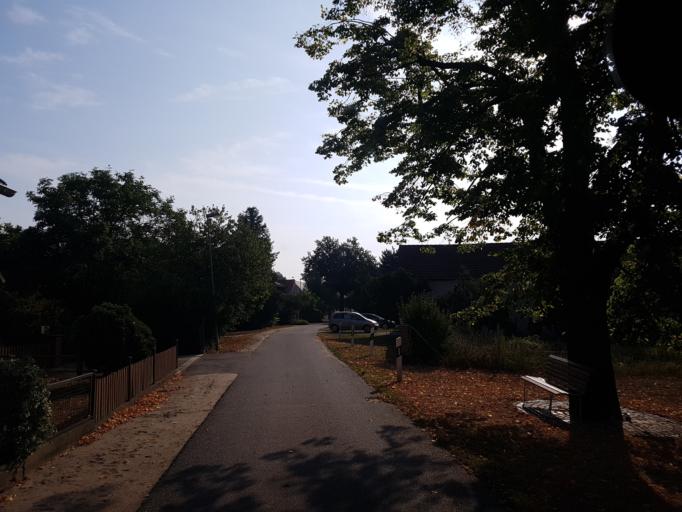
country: DE
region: Brandenburg
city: Finsterwalde
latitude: 51.6722
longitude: 13.7040
